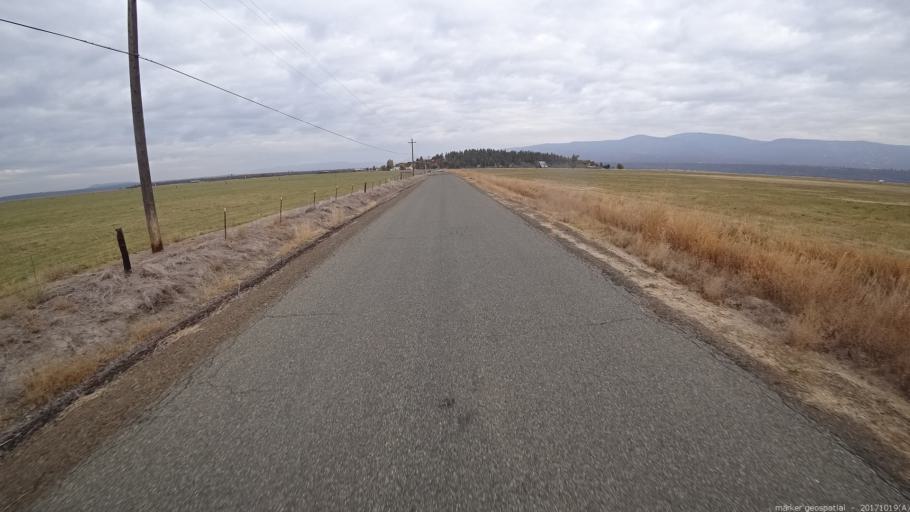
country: US
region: California
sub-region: Shasta County
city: Burney
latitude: 41.0855
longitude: -121.3652
